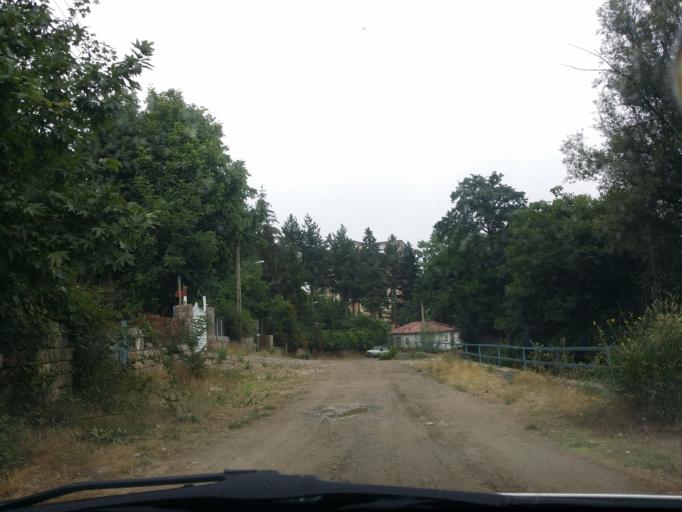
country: IR
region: Mazandaran
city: `Abbasabad
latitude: 36.5056
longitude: 51.1551
